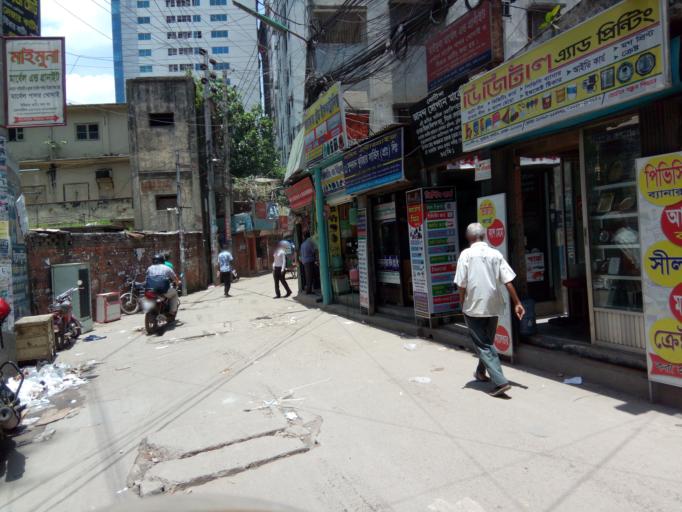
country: BD
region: Dhaka
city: Paltan
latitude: 23.7306
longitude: 90.4132
